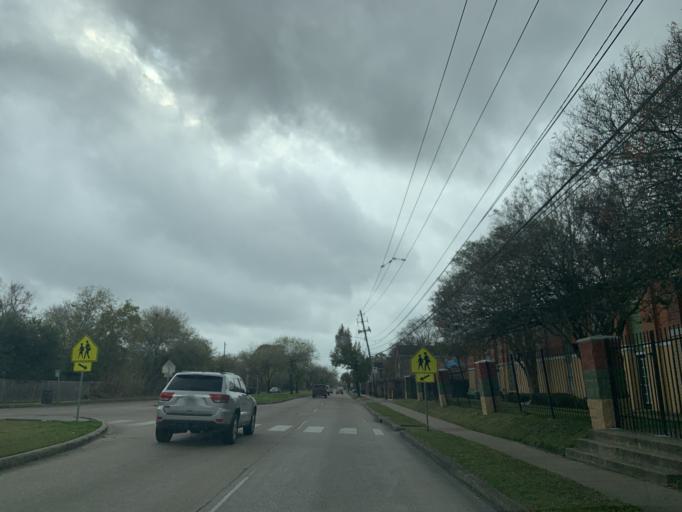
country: US
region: Texas
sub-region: Harris County
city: Bellaire
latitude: 29.6847
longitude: -95.5089
